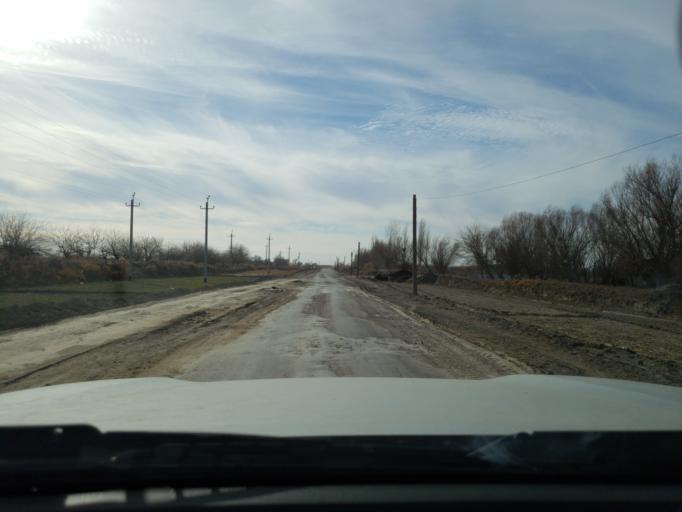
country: TM
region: Dasoguz
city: Dasoguz
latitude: 41.8466
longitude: 59.8777
